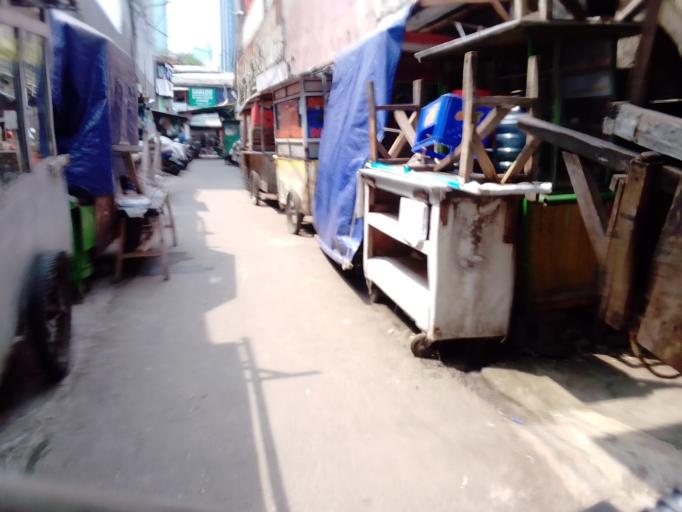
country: ID
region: Jakarta Raya
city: Jakarta
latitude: -6.2142
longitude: 106.8142
